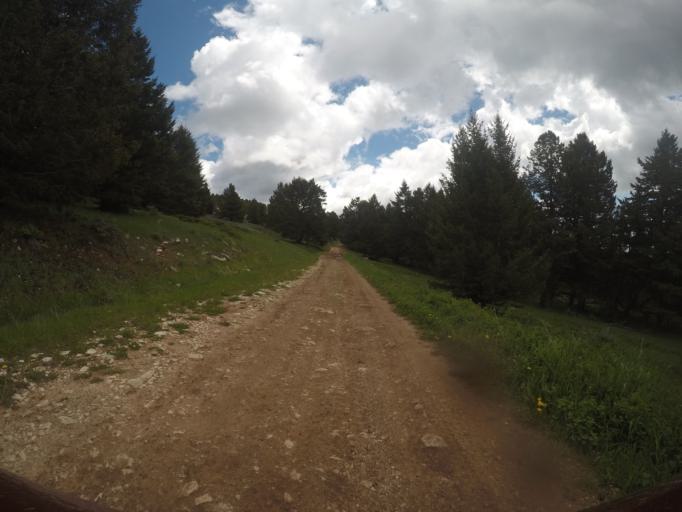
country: US
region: Wyoming
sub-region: Big Horn County
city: Lovell
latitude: 45.1718
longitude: -108.4330
